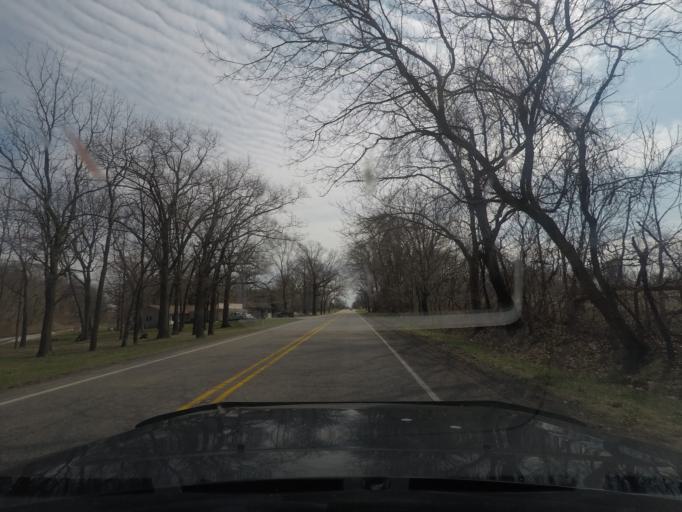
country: US
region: Indiana
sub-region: LaPorte County
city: Trail Creek
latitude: 41.6796
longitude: -86.7880
